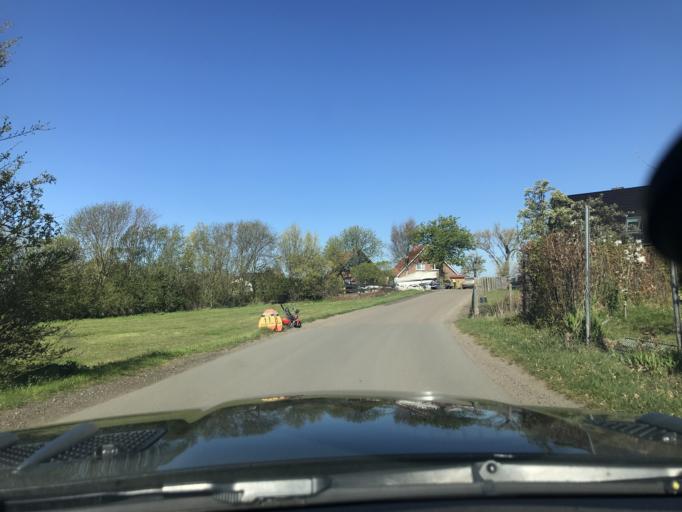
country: DE
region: Schleswig-Holstein
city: Grossenbrode
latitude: 54.4388
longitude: 11.1063
